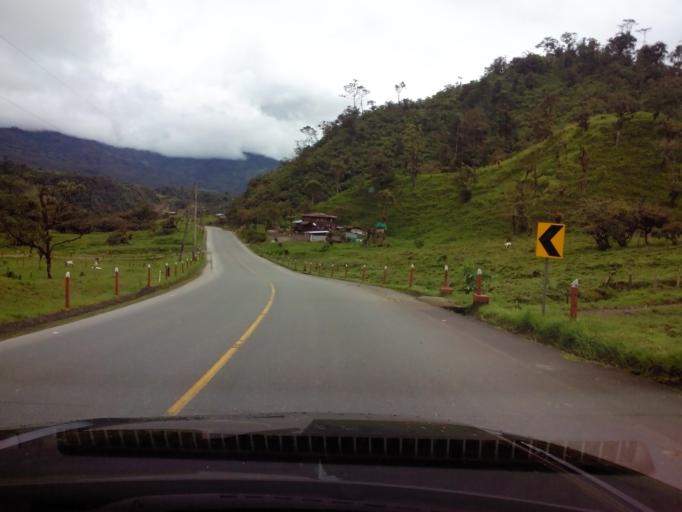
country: EC
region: Napo
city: Archidona
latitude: -0.5847
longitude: -77.8566
